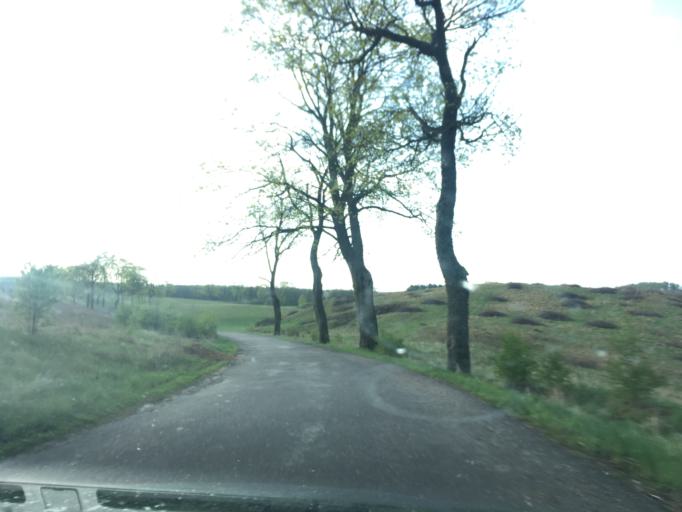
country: PL
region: Warmian-Masurian Voivodeship
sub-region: Powiat ostrodzki
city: Dabrowno
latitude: 53.4226
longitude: 20.0248
